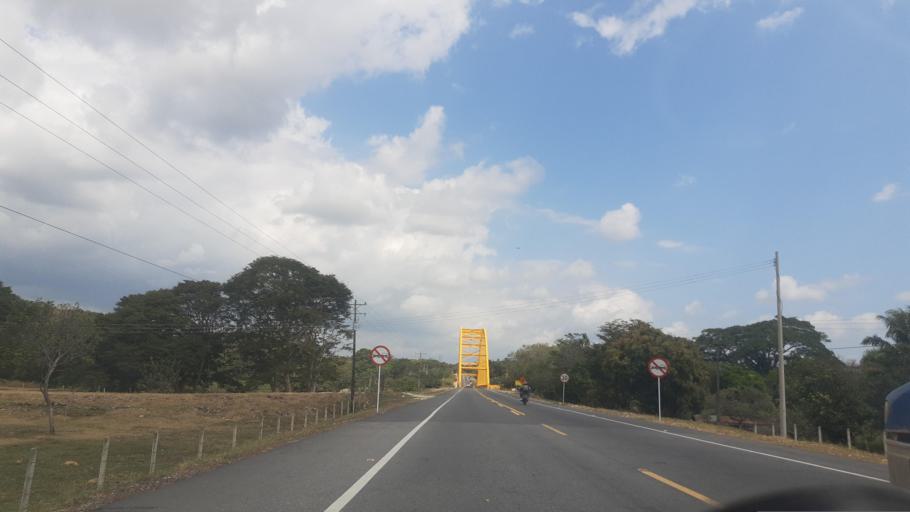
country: CO
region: Casanare
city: Tauramena
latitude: 4.9248
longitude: -72.6734
